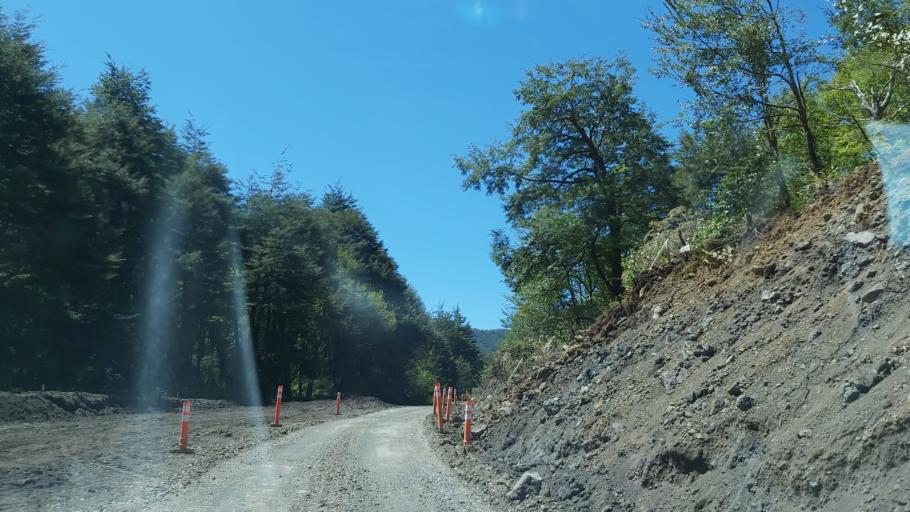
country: CL
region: Araucania
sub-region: Provincia de Cautin
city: Vilcun
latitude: -38.4705
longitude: -71.6756
